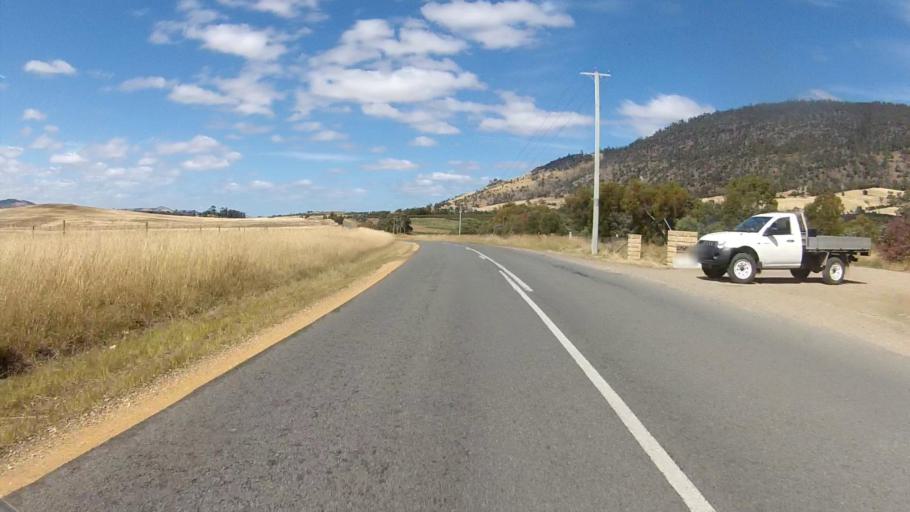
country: AU
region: Tasmania
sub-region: Sorell
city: Sorell
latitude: -42.6239
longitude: 147.4290
